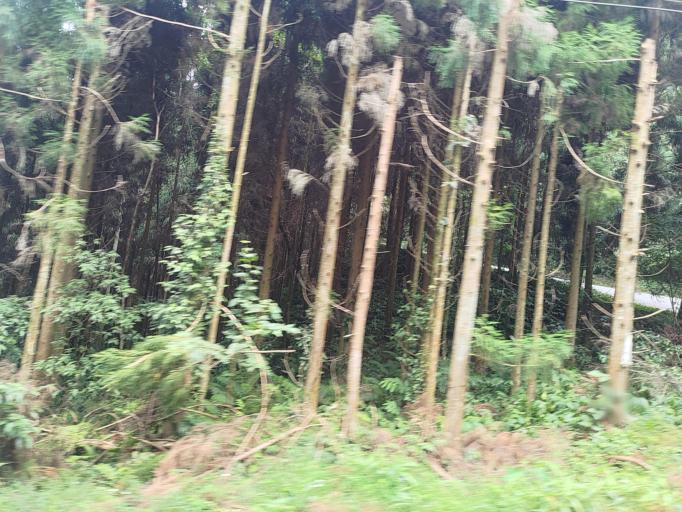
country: TW
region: Taiwan
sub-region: Hsinchu
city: Hsinchu
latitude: 24.6284
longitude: 121.0772
